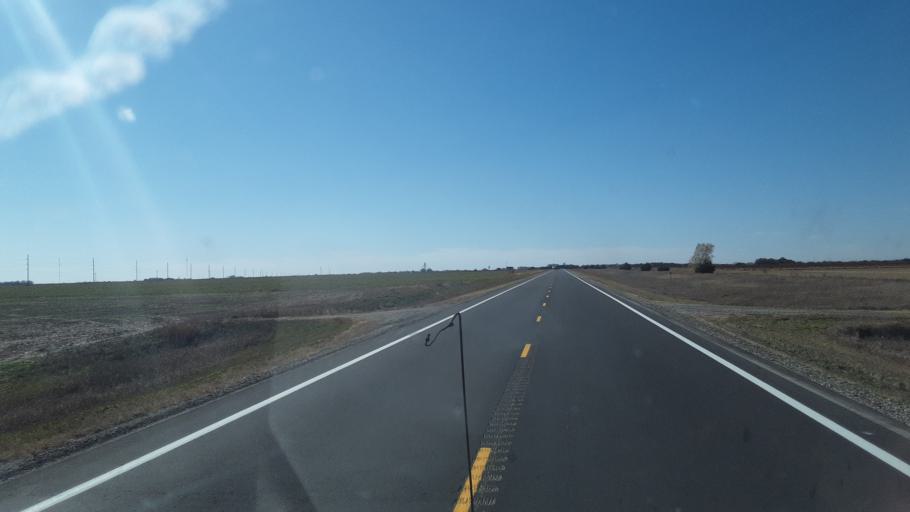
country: US
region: Kansas
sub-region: Rice County
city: Lyons
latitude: 38.3677
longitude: -98.1516
